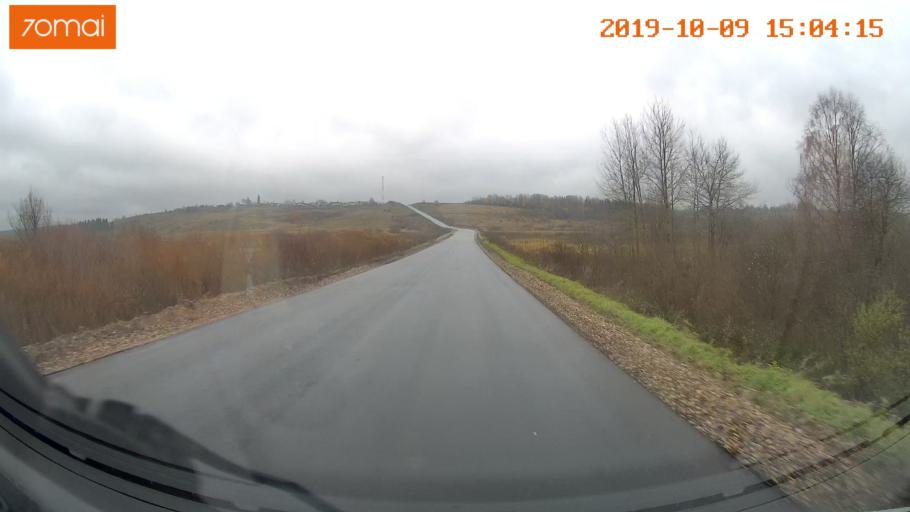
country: RU
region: Kostroma
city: Chistyye Bory
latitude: 58.2610
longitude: 41.6689
